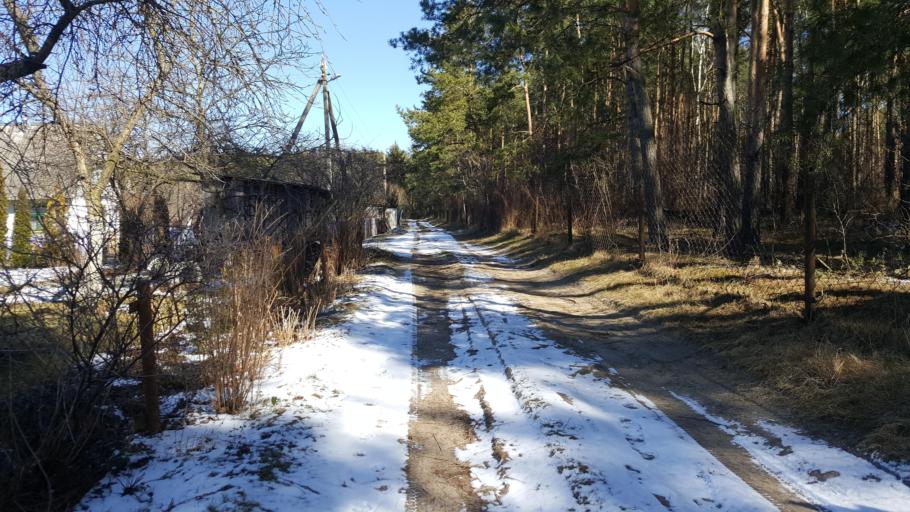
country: BY
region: Brest
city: Kamyanyets
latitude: 52.3661
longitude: 23.8079
